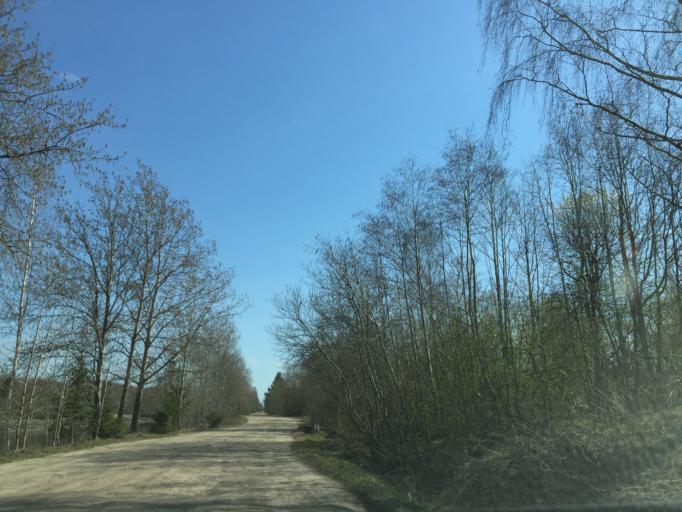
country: EE
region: Ida-Virumaa
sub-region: Narva linn
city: Narva
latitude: 59.3527
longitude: 28.1490
